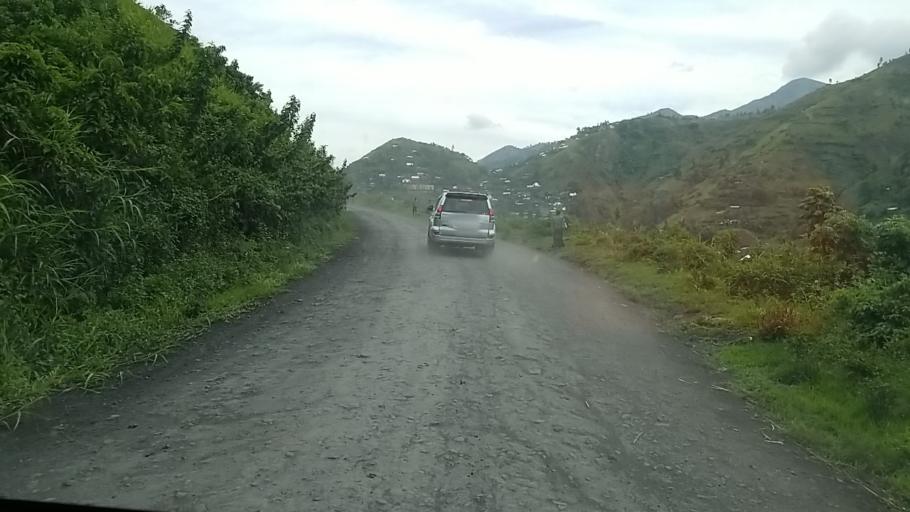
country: CD
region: Nord Kivu
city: Sake
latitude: -1.7499
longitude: 28.9876
